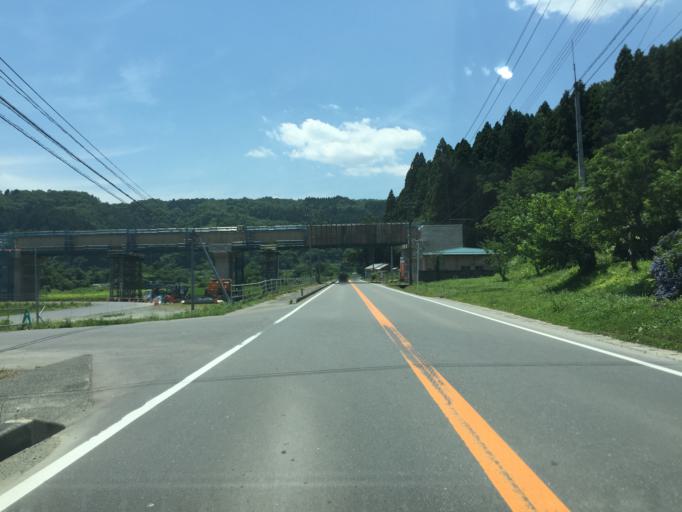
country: JP
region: Miyagi
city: Marumori
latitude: 37.7687
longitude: 140.8603
